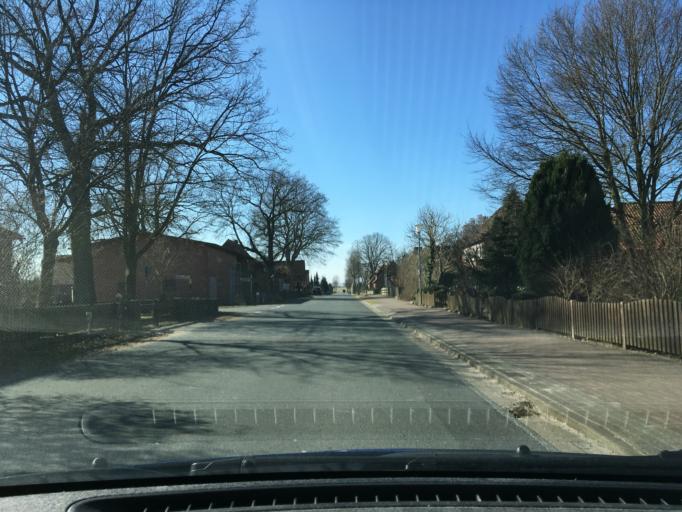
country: DE
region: Lower Saxony
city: Egestorf
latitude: 53.1507
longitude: 10.0659
